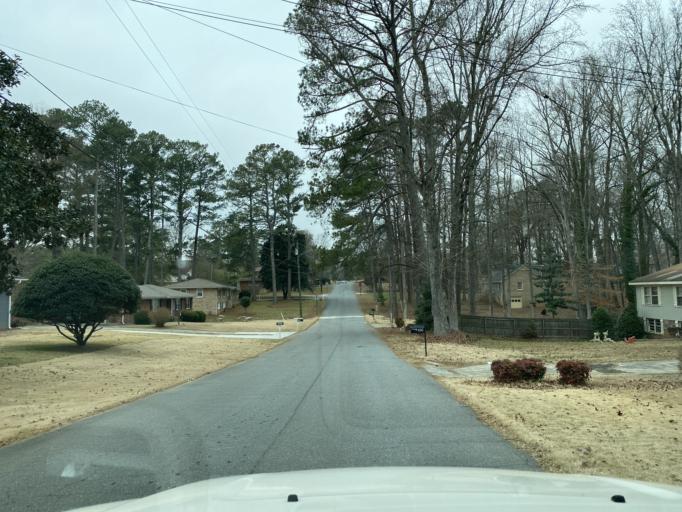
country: US
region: Georgia
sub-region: Cobb County
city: Fair Oaks
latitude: 33.9211
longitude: -84.5842
